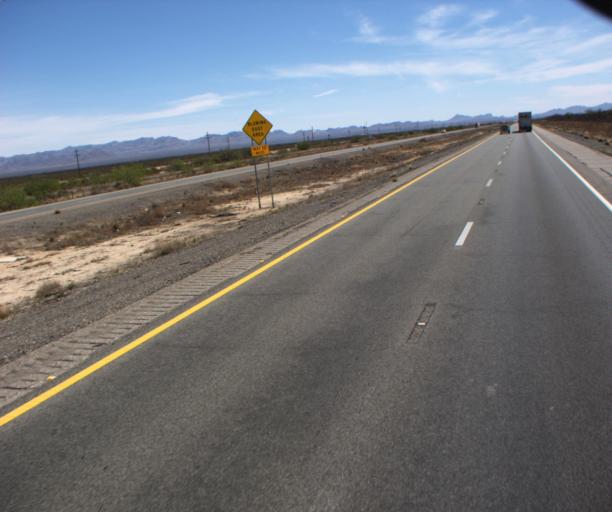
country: US
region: Arizona
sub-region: Cochise County
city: Willcox
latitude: 32.2881
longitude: -109.3146
